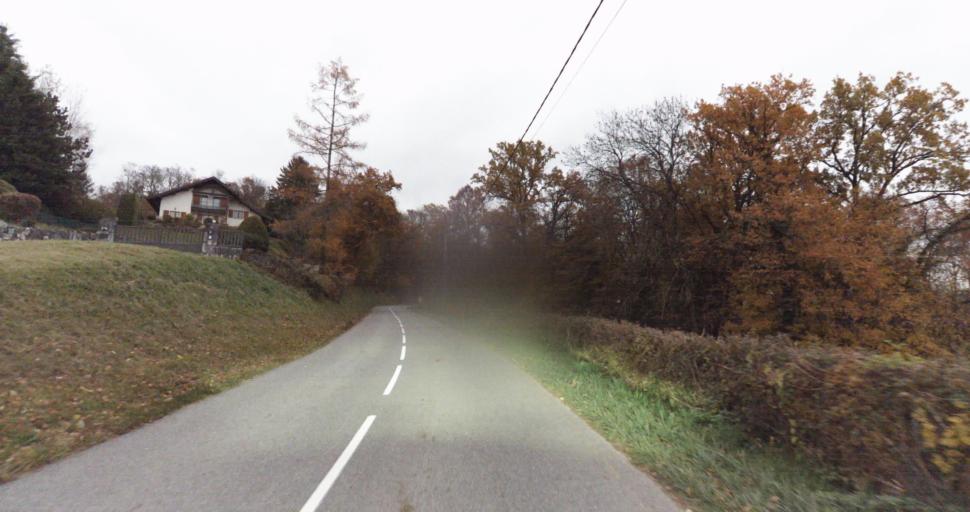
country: FR
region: Rhone-Alpes
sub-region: Departement de la Haute-Savoie
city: Alby-sur-Cheran
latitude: 45.8421
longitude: 6.0020
